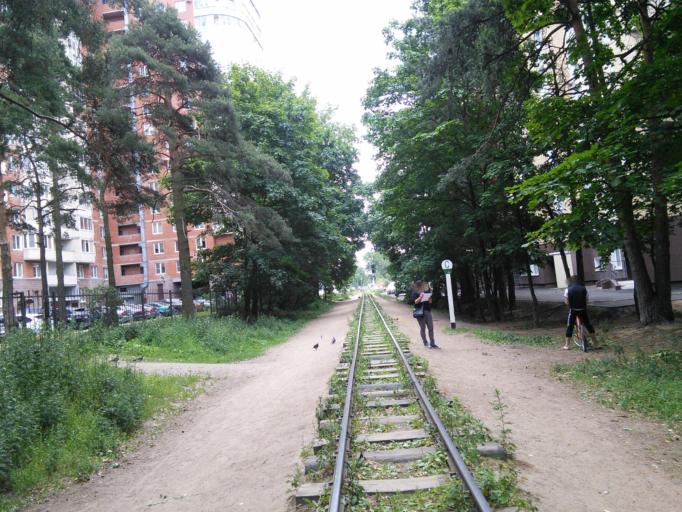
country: RU
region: St.-Petersburg
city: Kolomyagi
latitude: 60.0291
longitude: 30.2932
